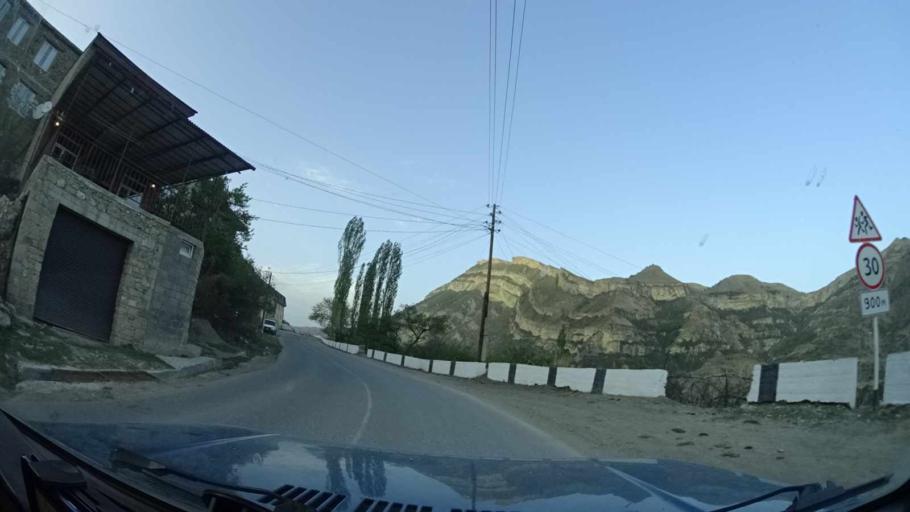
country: RU
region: Dagestan
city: Gunib
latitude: 42.3820
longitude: 46.9636
